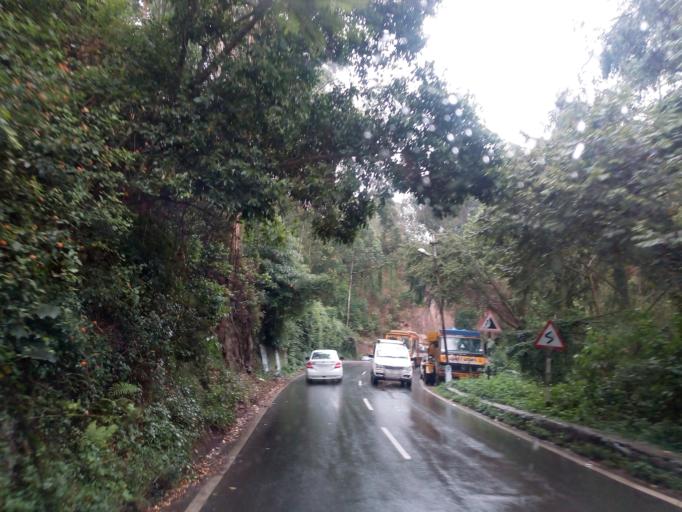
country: IN
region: Tamil Nadu
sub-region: Nilgiri
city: Wellington
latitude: 11.3456
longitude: 76.7899
